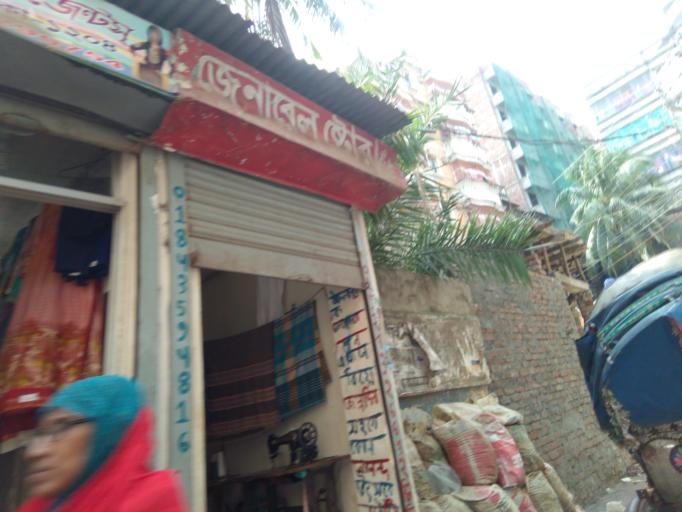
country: BD
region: Dhaka
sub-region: Dhaka
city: Dhaka
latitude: 23.7006
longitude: 90.4239
